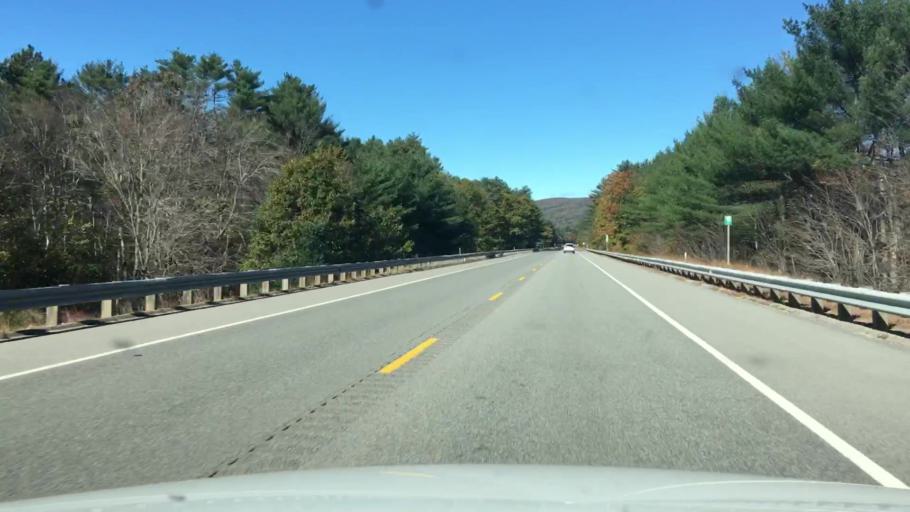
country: US
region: New Hampshire
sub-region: Carroll County
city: Sanbornville
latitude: 43.4899
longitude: -71.0143
